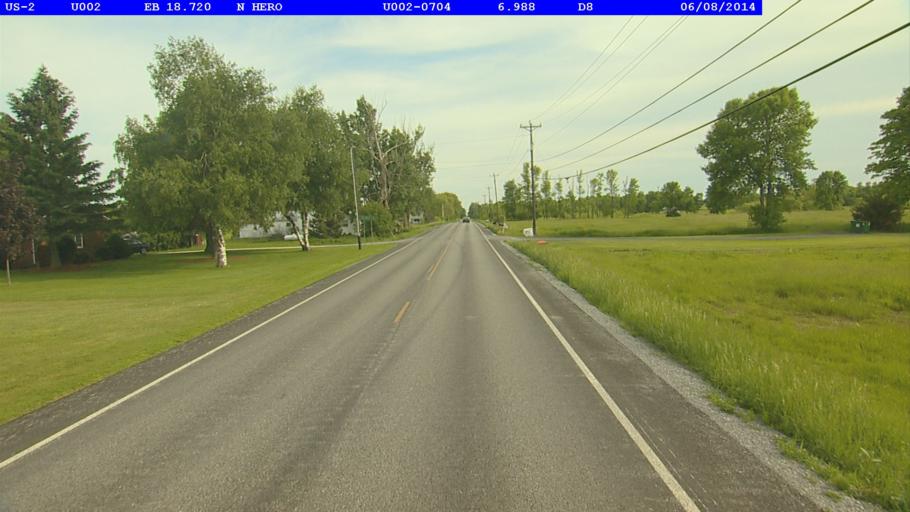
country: US
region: Vermont
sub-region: Grand Isle County
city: North Hero
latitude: 44.7989
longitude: -73.2922
